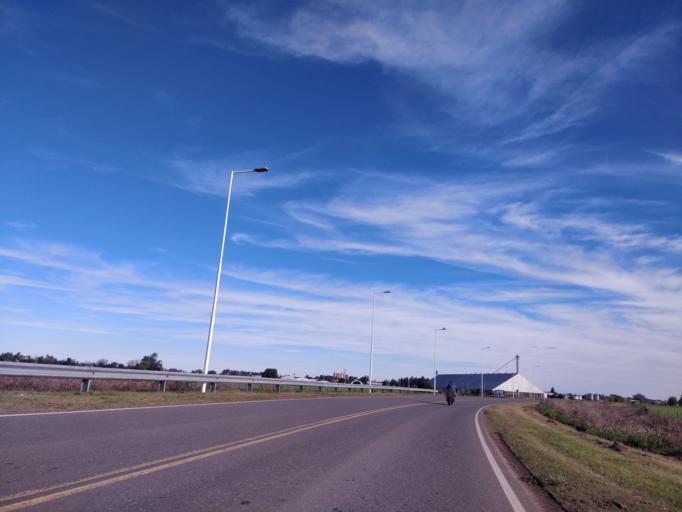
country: AR
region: Cordoba
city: Leones
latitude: -32.6469
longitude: -62.2917
